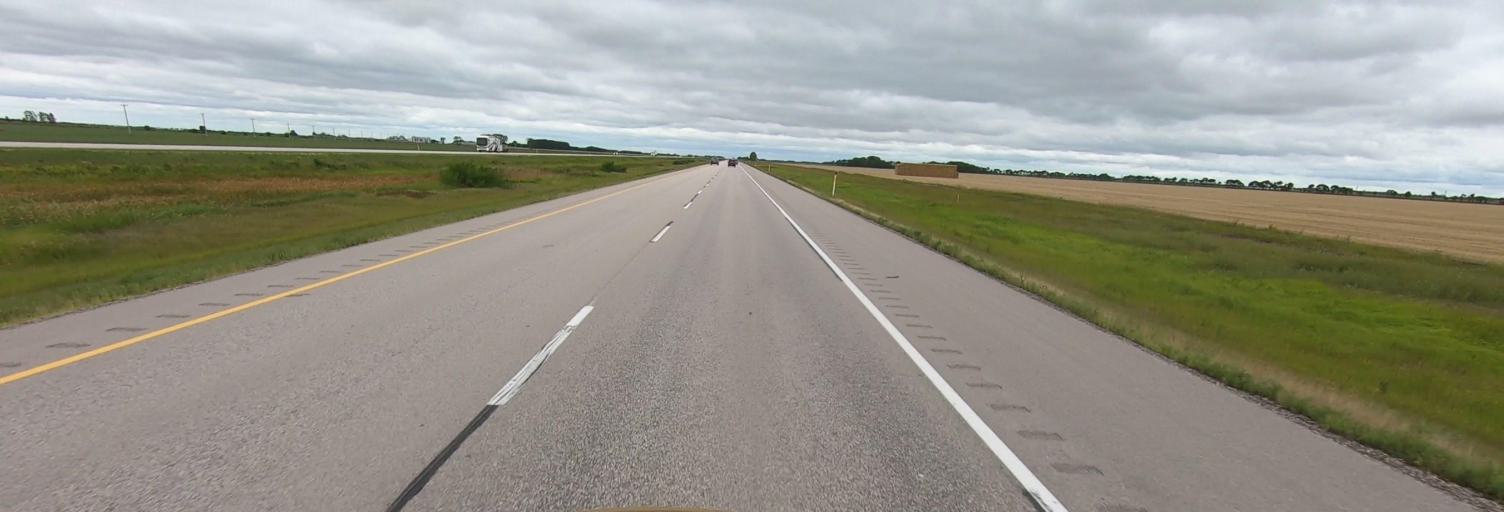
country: CA
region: Manitoba
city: Headingley
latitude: 49.9169
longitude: -97.8104
